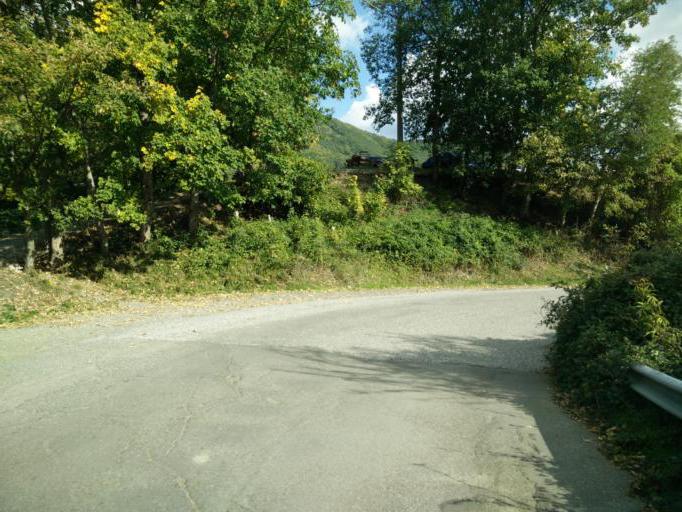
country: IT
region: Tuscany
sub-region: Provincia di Massa-Carrara
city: Zeri
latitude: 44.3576
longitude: 9.7588
